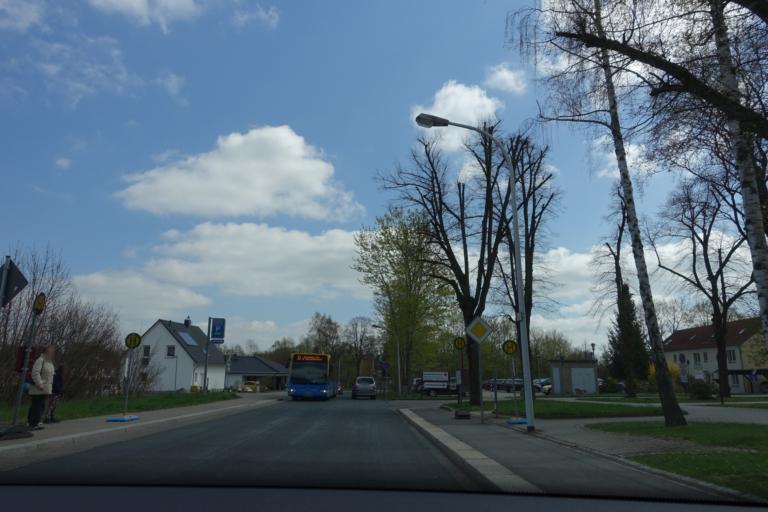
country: DE
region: Saxony
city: Neukirchen
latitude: 50.8219
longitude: 12.8259
